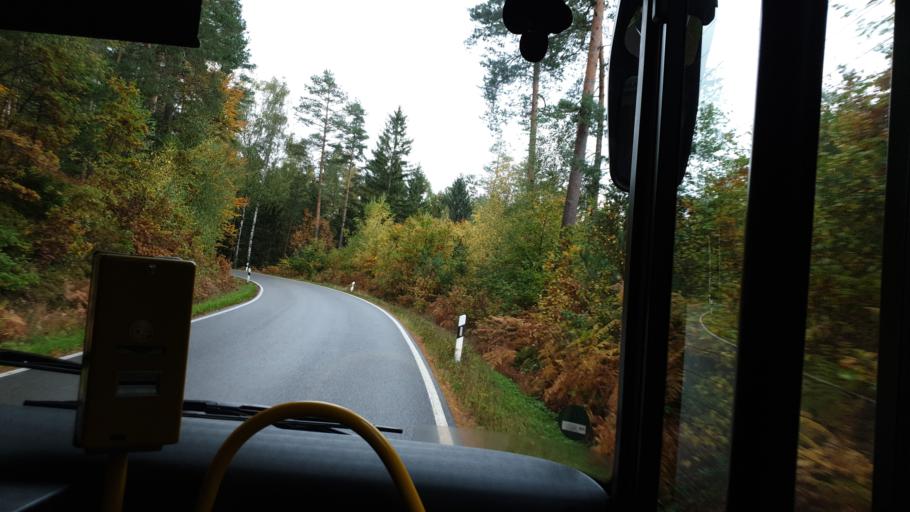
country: DE
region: Saxony
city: Kurort Gohrisch
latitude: 50.8919
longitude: 14.1008
